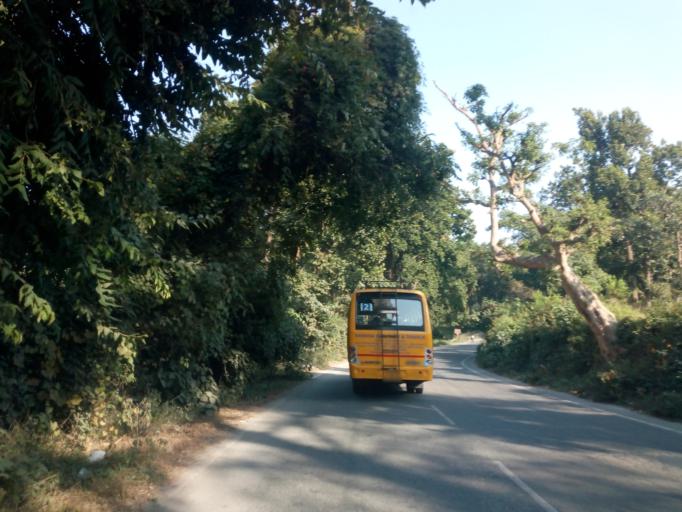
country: IN
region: Uttarakhand
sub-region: Dehradun
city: Dehradun
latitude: 30.3488
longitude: 77.8899
